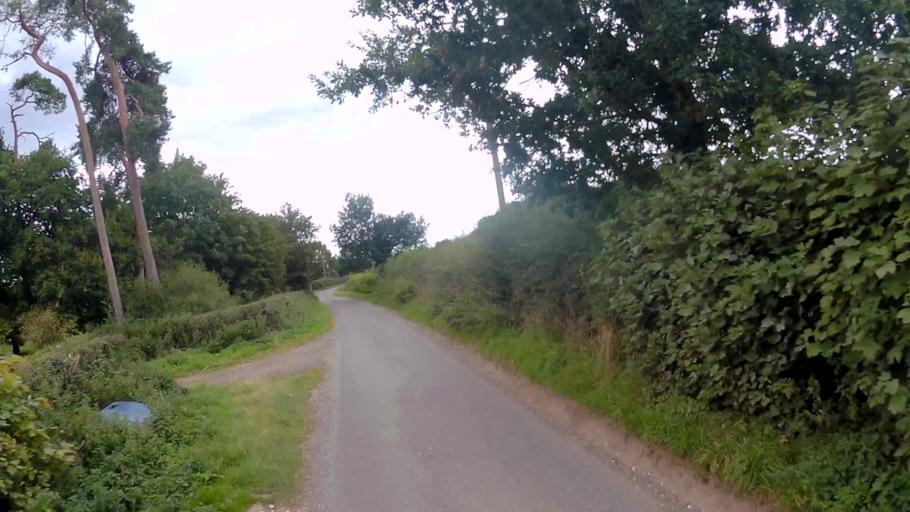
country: GB
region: England
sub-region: Hampshire
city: Overton
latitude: 51.2081
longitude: -1.2332
